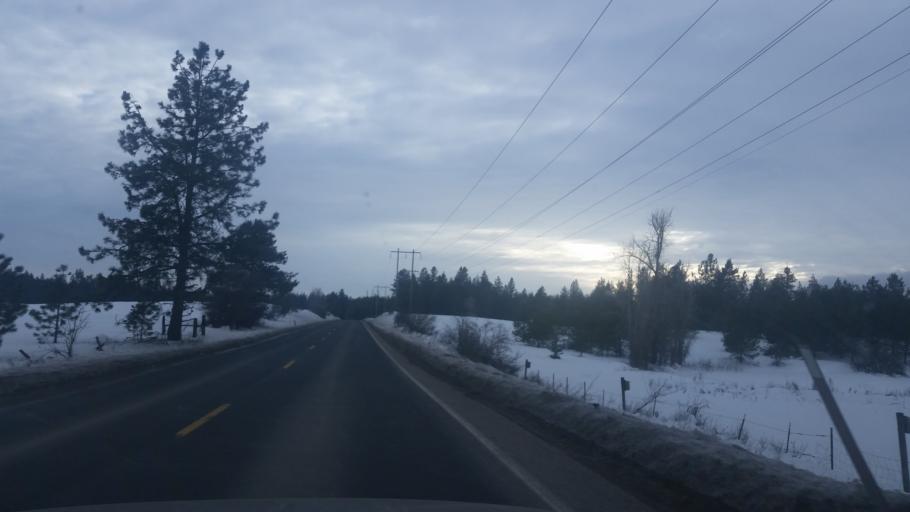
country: US
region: Washington
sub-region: Stevens County
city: Chewelah
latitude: 48.0850
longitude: -117.7580
